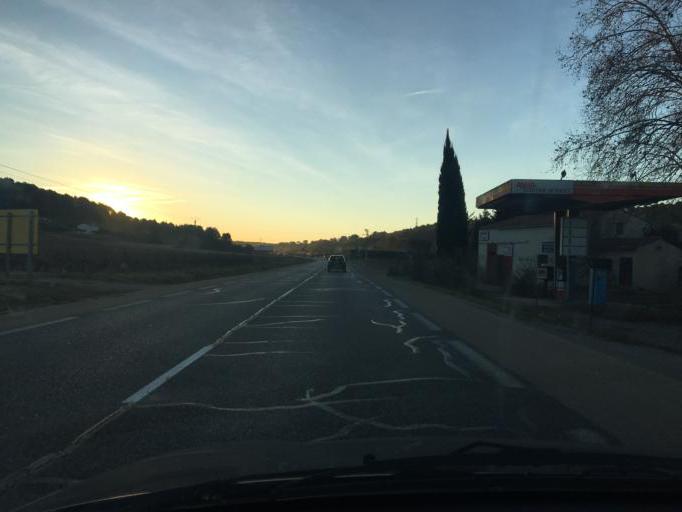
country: FR
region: Provence-Alpes-Cote d'Azur
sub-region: Departement du Var
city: Lorgues
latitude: 43.4769
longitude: 6.3740
